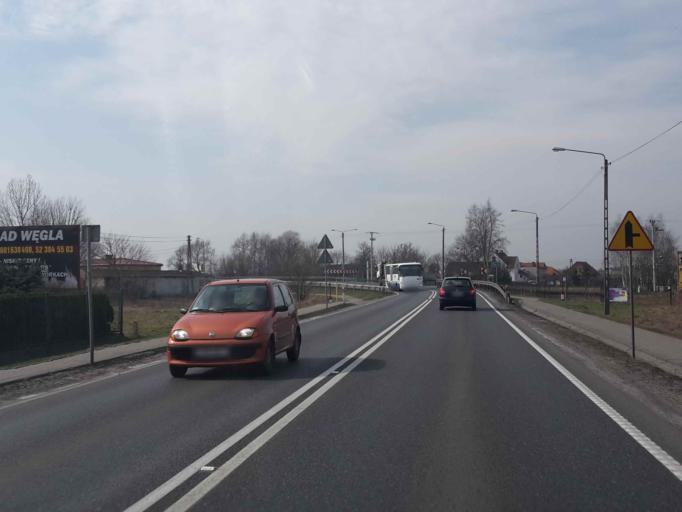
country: PL
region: Kujawsko-Pomorskie
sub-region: Powiat bydgoski
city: Biale Blota
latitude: 53.0722
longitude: 17.8216
